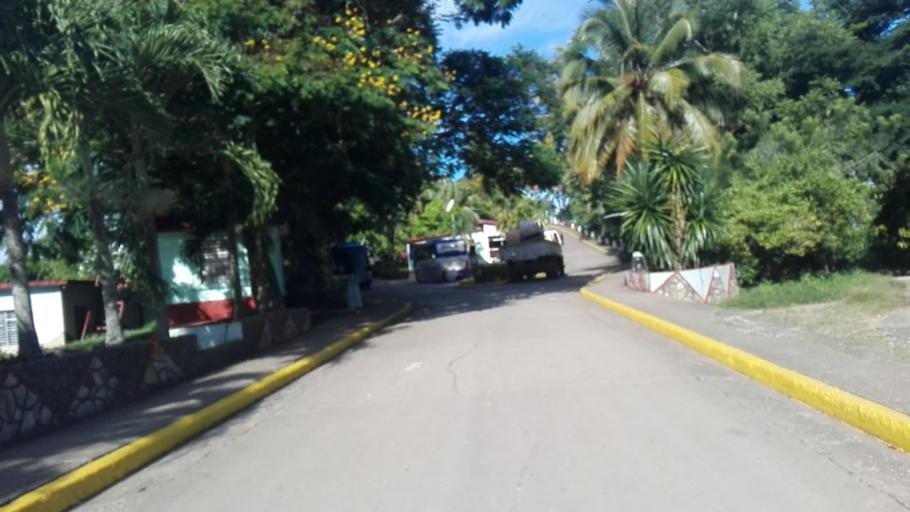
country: CU
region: Granma
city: Bartolome Maso
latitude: 20.1580
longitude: -76.9491
